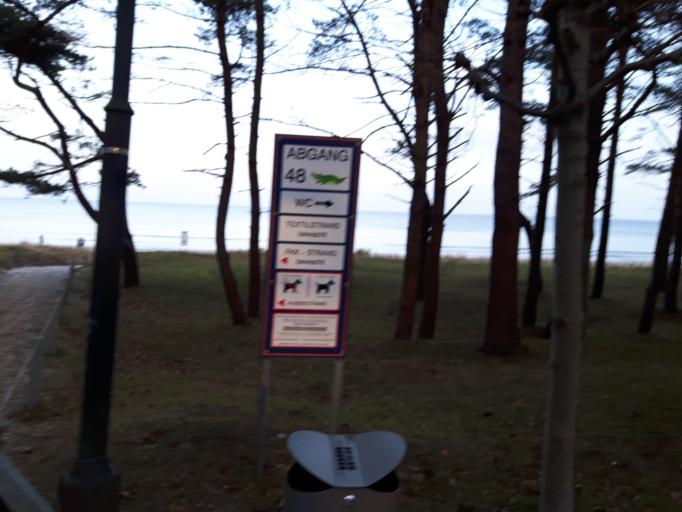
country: DE
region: Mecklenburg-Vorpommern
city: Ostseebad Binz
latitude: 54.4141
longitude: 13.5973
